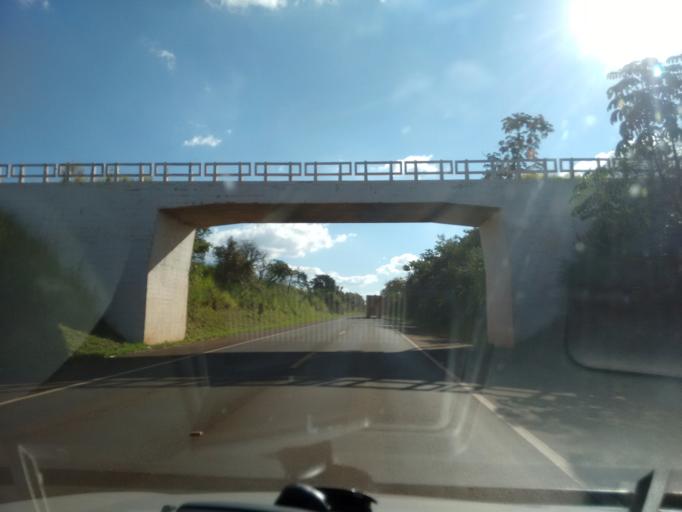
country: BR
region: Sao Paulo
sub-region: Americo Brasiliense
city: Americo Brasiliense
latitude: -21.6222
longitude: -48.0119
